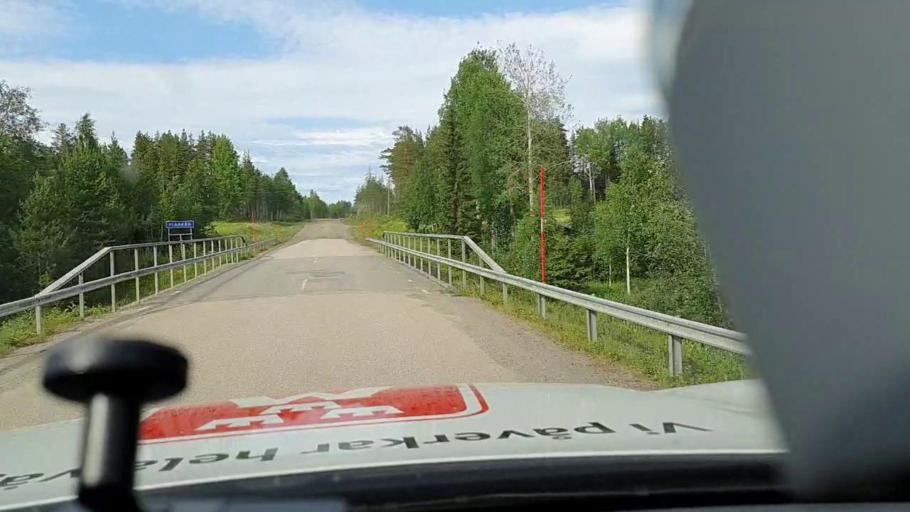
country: SE
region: Norrbotten
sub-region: Alvsbyns Kommun
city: AElvsbyn
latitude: 66.1500
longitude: 21.0309
